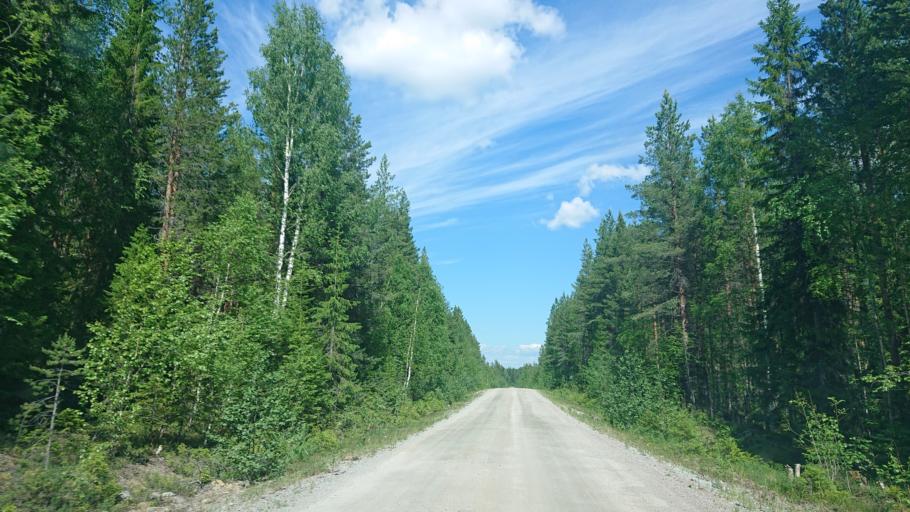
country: SE
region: Vaesternorrland
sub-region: Solleftea Kommun
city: Solleftea
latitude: 62.9520
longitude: 17.1409
